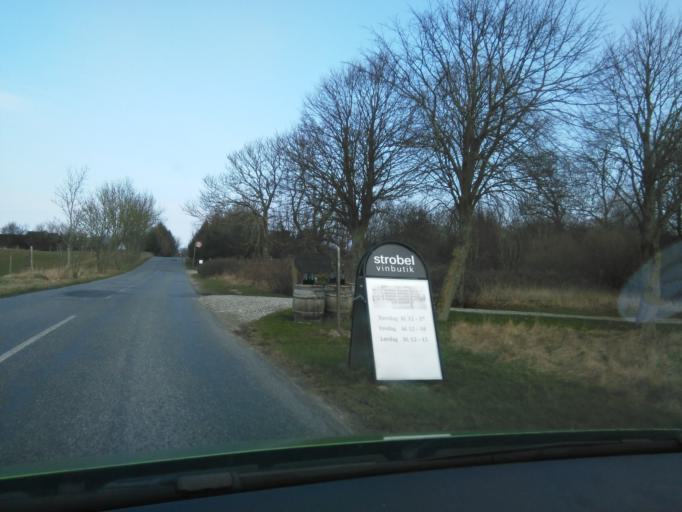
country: DK
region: Central Jutland
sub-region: Arhus Kommune
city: Beder
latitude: 56.0535
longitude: 10.2415
